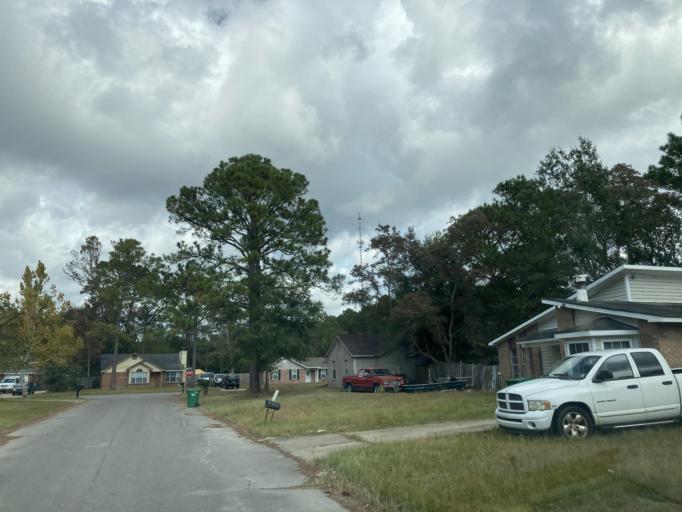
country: US
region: Mississippi
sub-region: Jackson County
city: Gulf Hills
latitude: 30.4463
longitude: -88.8268
